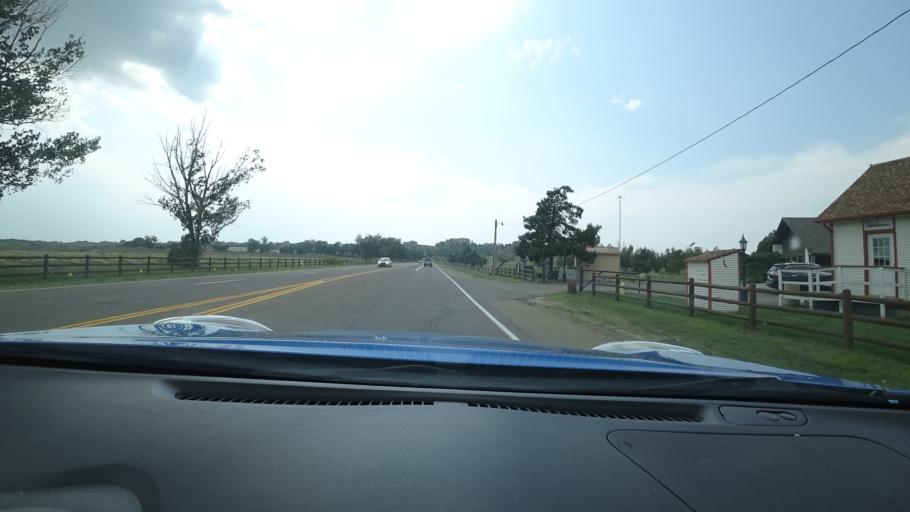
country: US
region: Colorado
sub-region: Adams County
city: Todd Creek
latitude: 39.9252
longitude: -104.8777
